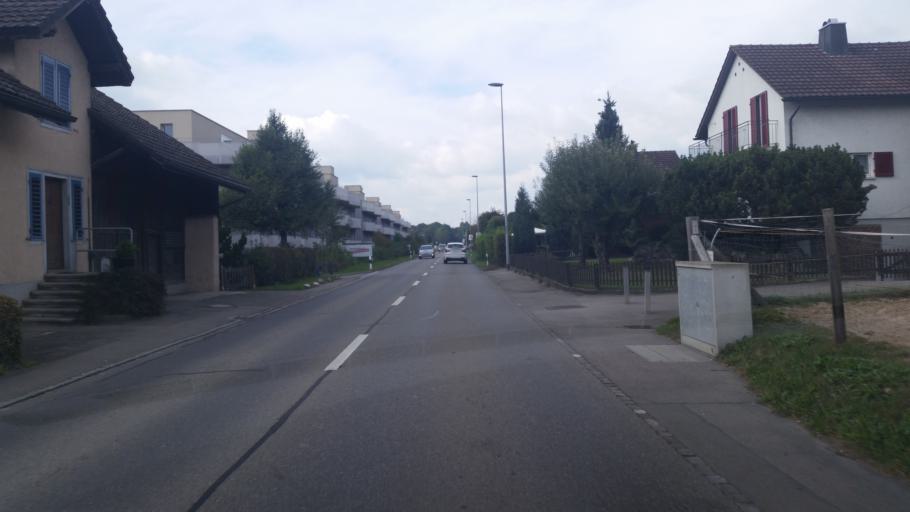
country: CH
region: Aargau
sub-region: Bezirk Bremgarten
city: Wohlen
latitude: 47.3655
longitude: 8.2617
